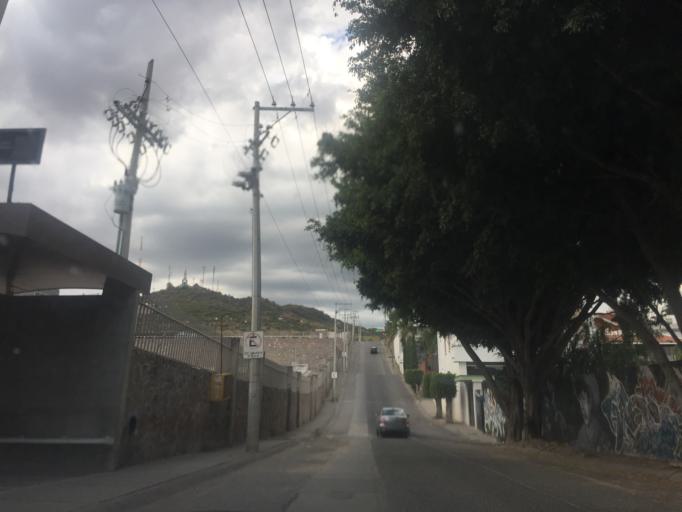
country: MX
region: Guanajuato
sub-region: Leon
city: La Ermita
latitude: 21.1530
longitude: -101.7095
